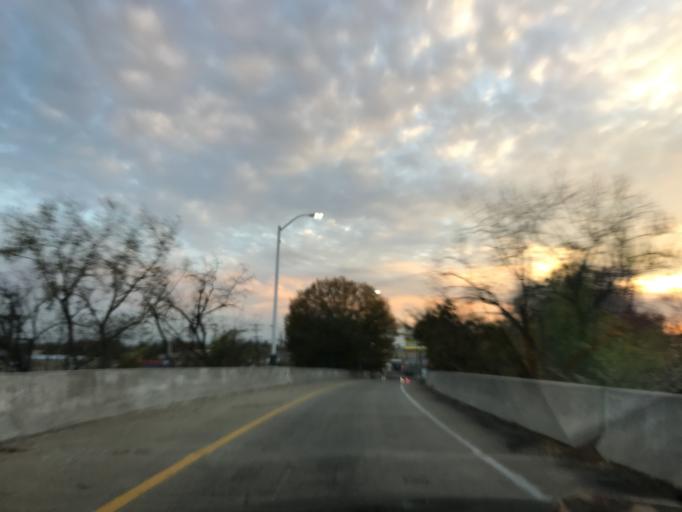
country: US
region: Maryland
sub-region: Baltimore County
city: Rosedale
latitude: 39.3058
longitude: -76.5381
